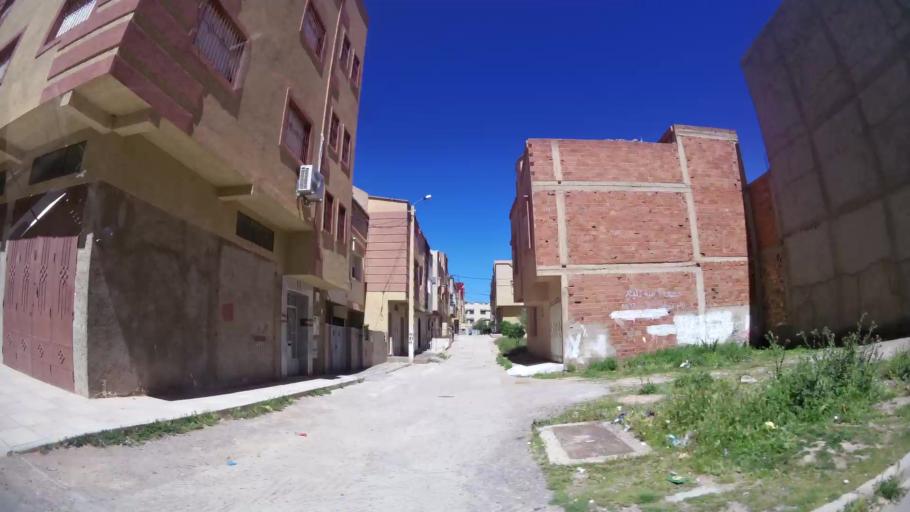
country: MA
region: Oriental
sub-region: Oujda-Angad
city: Oujda
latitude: 34.6630
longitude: -1.8722
